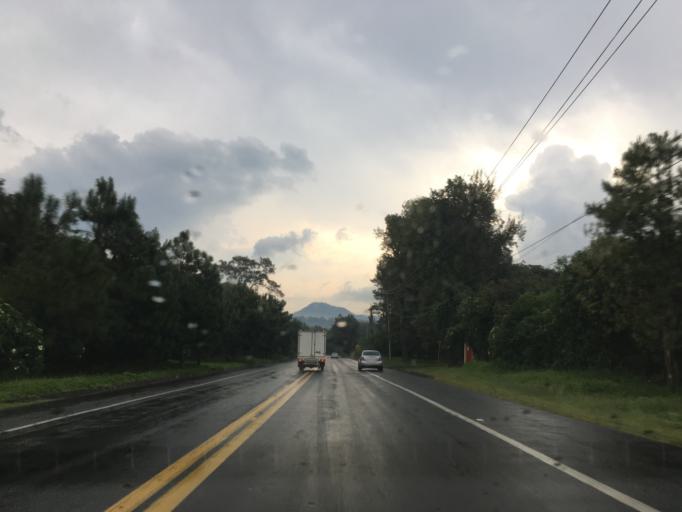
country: MX
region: Michoacan
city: Capacuaro
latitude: 19.5074
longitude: -102.0781
